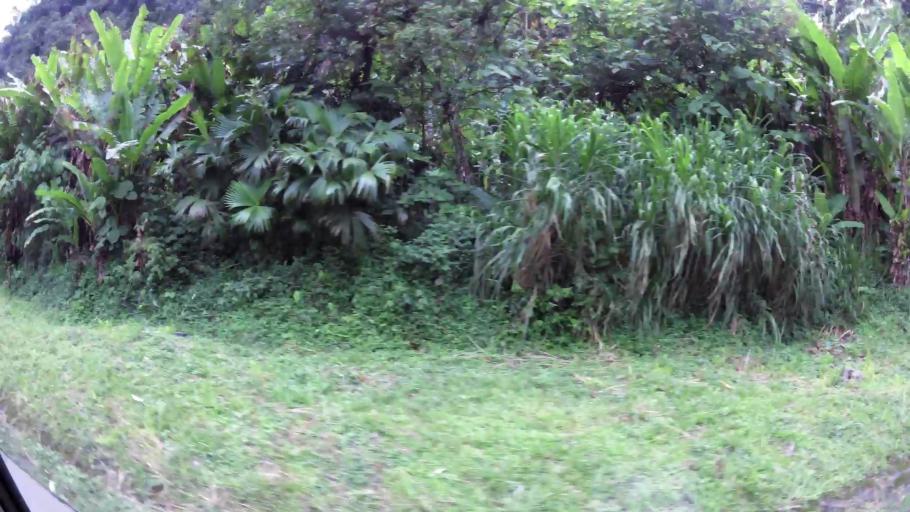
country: EC
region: Santo Domingo de los Tsachilas
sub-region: Canton Santo Domingo de los Colorados
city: Santo Domingo de los Colorados
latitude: -0.2722
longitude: -79.0811
